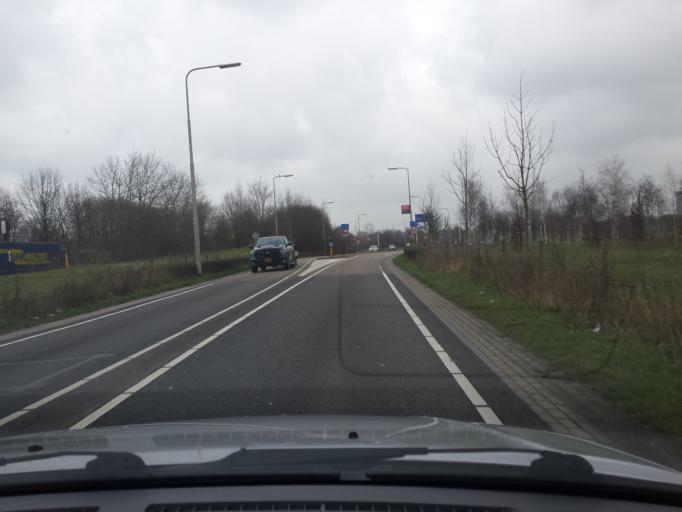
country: NL
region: Limburg
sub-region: Gemeente Sittard-Geleen
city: Limbricht
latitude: 50.9842
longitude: 5.8376
